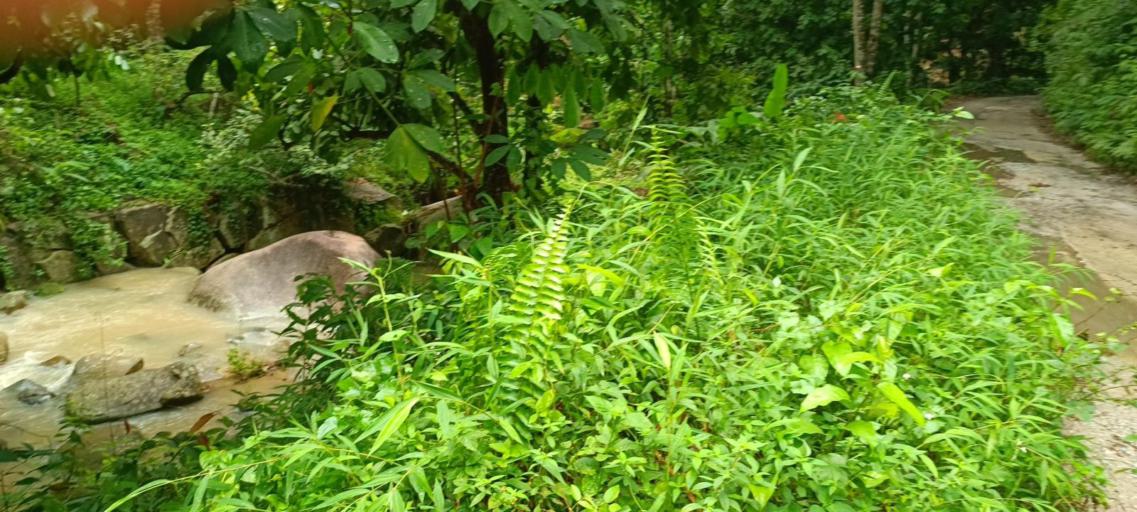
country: MY
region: Penang
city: Kampung Sungai Ara
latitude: 5.3238
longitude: 100.2524
